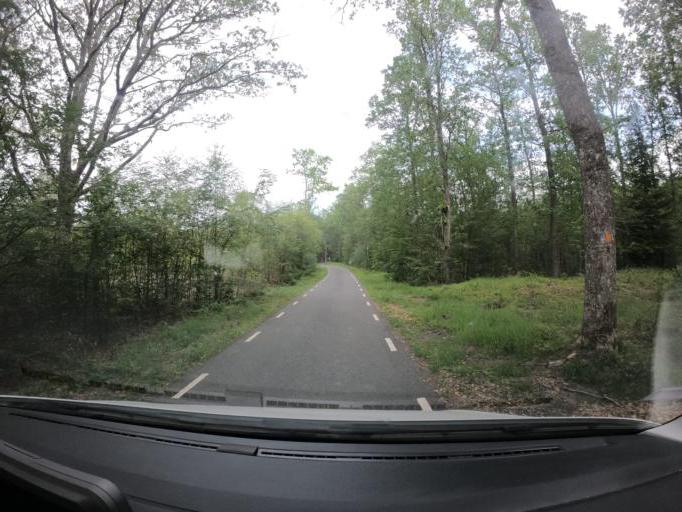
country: SE
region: Skane
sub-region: Eslovs Kommun
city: Stehag
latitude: 56.0061
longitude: 13.3933
